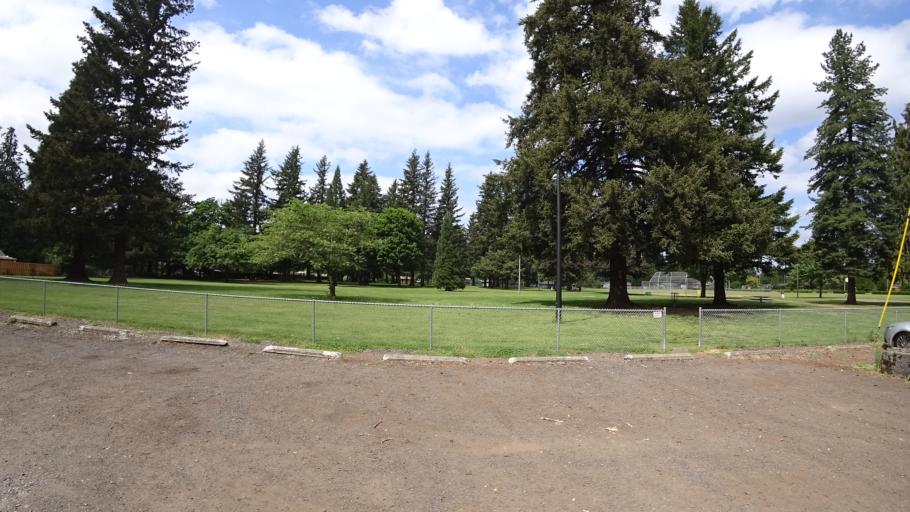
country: US
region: Oregon
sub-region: Multnomah County
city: Gresham
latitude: 45.5137
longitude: -122.4814
